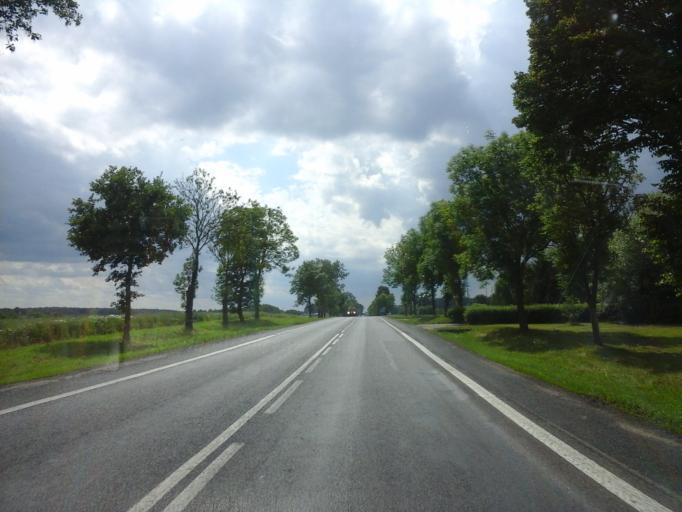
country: PL
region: West Pomeranian Voivodeship
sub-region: Powiat bialogardzki
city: Karlino
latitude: 54.0596
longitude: 15.9322
